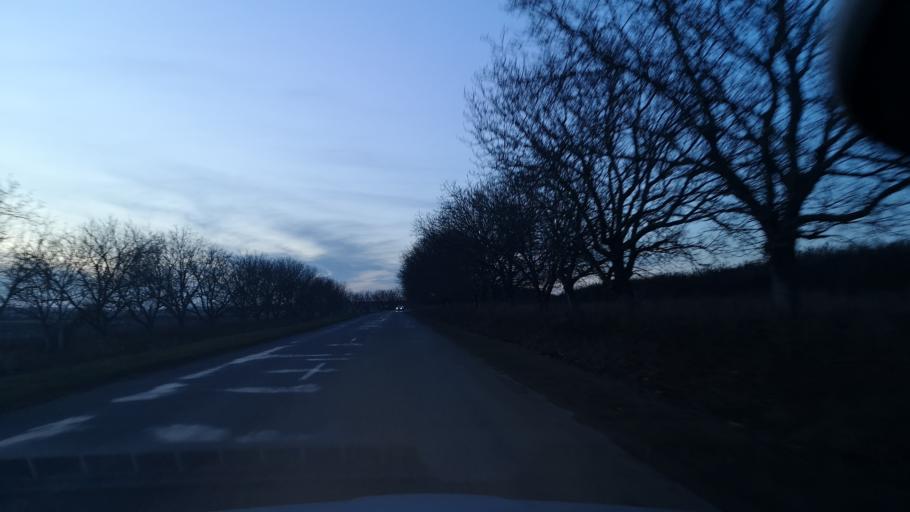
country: MD
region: Orhei
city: Orhei
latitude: 47.2849
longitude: 28.8290
